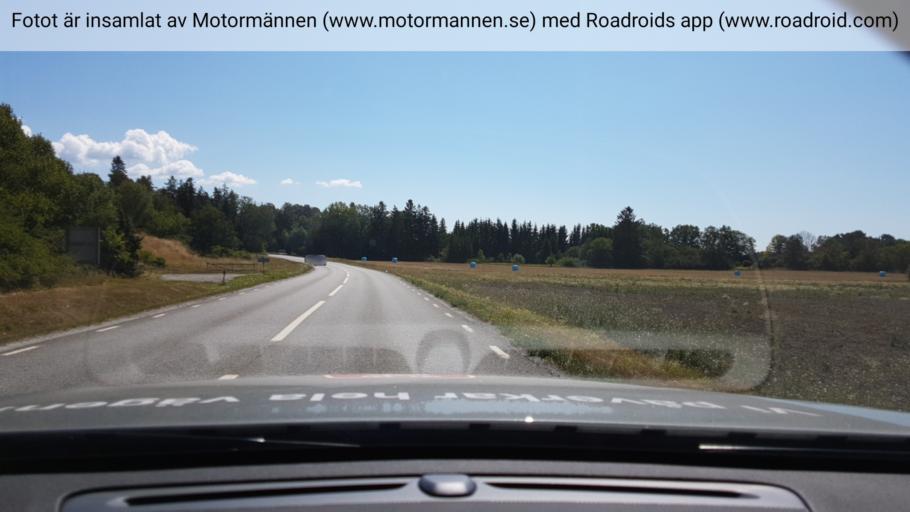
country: SE
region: Stockholm
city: Stenhamra
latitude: 59.3413
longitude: 17.7267
